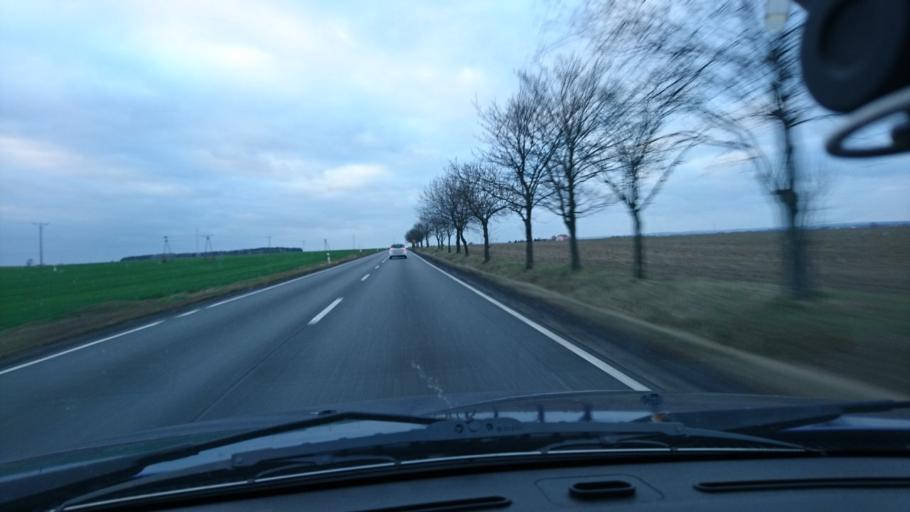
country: PL
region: Greater Poland Voivodeship
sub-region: Powiat kepinski
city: Slupia pod Kepnem
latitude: 51.2437
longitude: 18.0255
